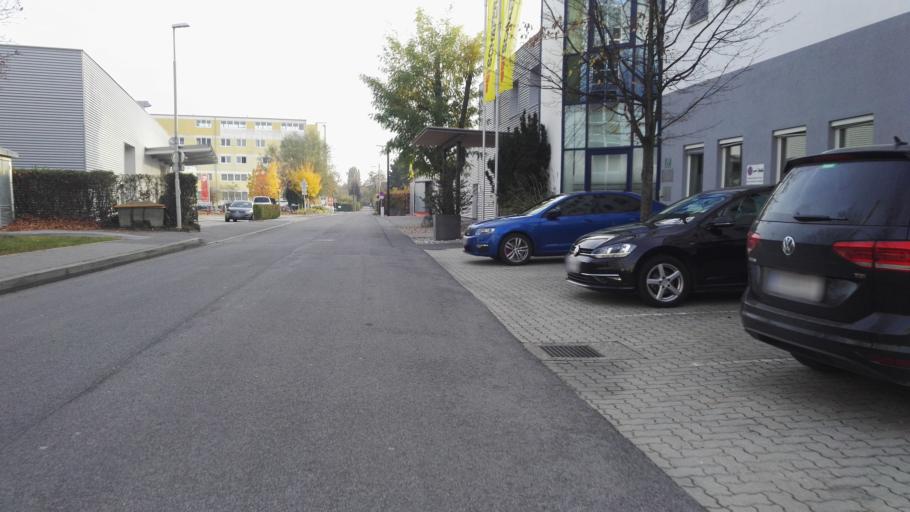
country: AT
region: Styria
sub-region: Graz Stadt
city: Goesting
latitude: 47.0965
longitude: 15.4091
